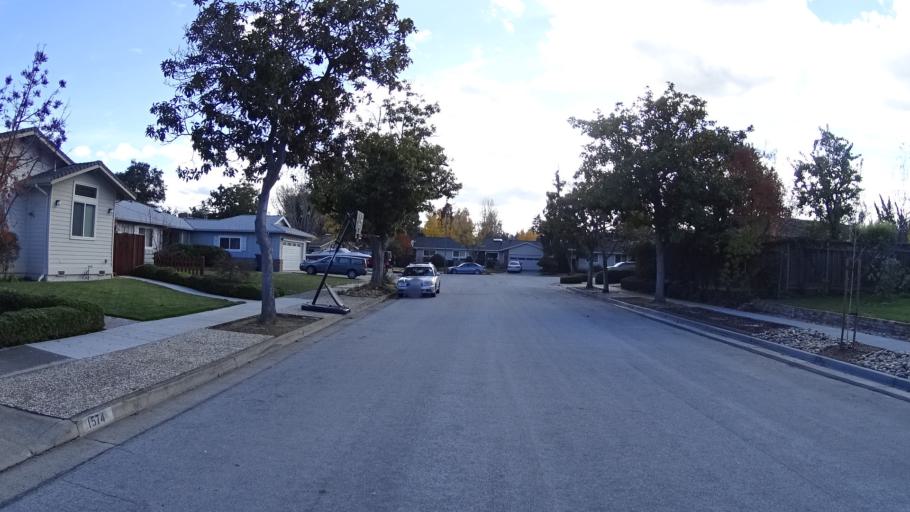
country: US
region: California
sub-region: Santa Clara County
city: Cupertino
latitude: 37.3424
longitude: -122.0522
